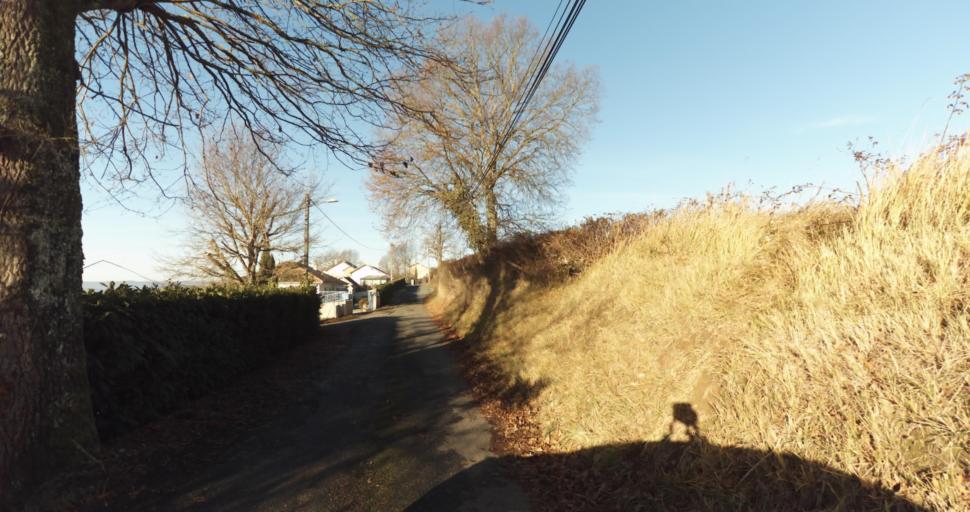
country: FR
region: Limousin
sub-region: Departement de la Haute-Vienne
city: Aixe-sur-Vienne
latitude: 45.7999
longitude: 1.1449
